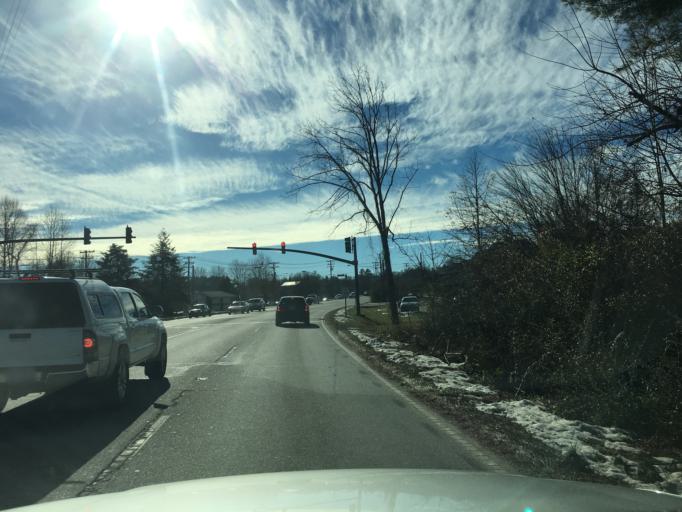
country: US
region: North Carolina
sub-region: Transylvania County
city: Brevard
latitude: 35.2433
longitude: -82.7248
